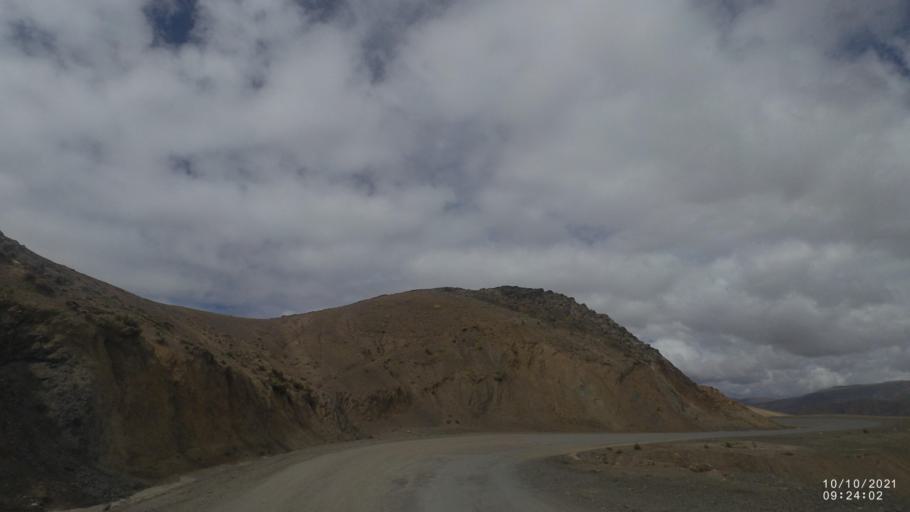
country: BO
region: La Paz
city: Quime
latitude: -17.0879
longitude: -67.3077
